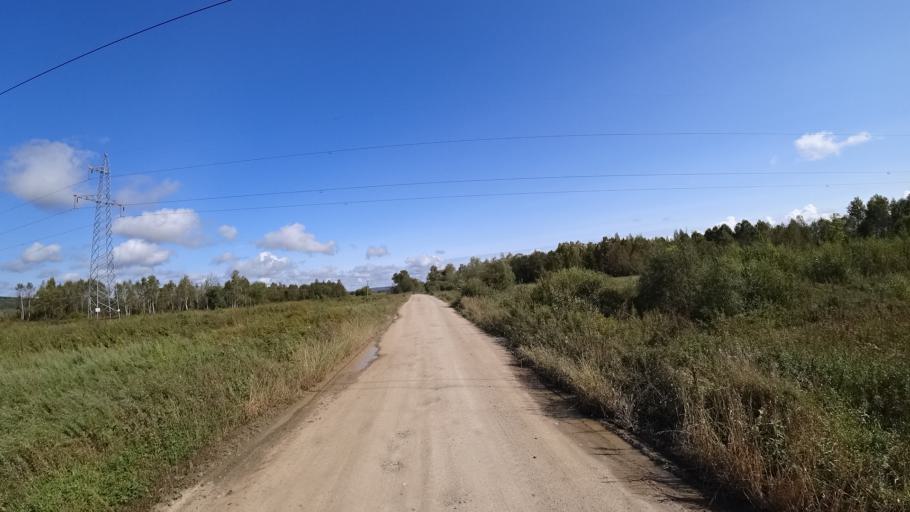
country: RU
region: Amur
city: Arkhara
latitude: 49.4089
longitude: 130.1615
